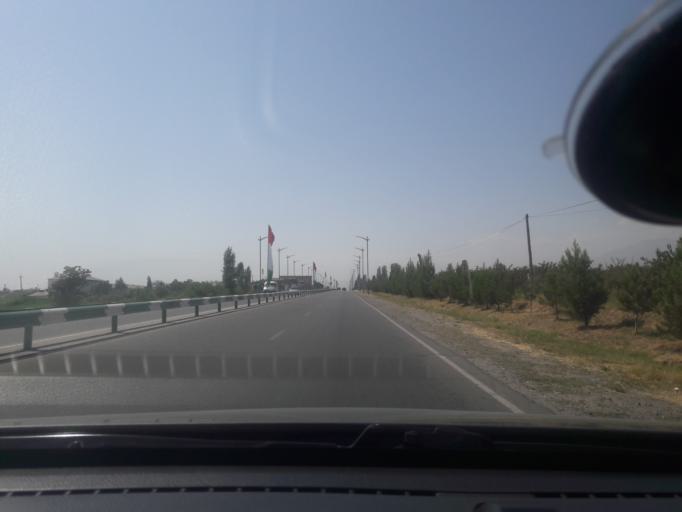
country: TJ
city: Shahrinav
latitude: 38.5617
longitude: 68.4256
